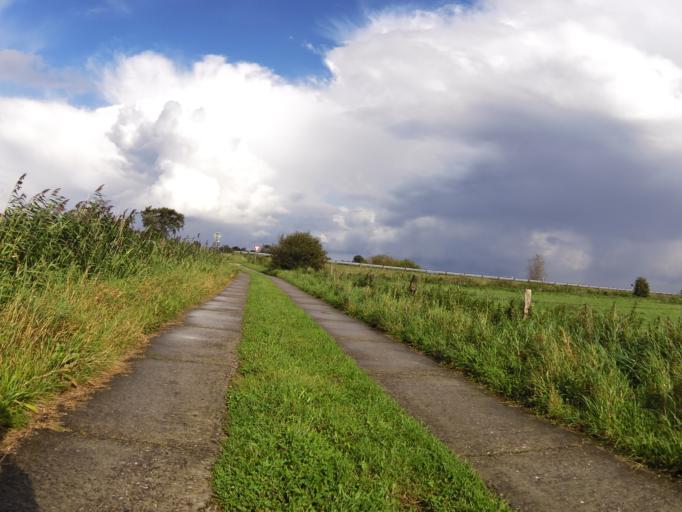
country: DE
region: Schleswig-Holstein
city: Wisch
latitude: 54.4211
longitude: 10.3854
